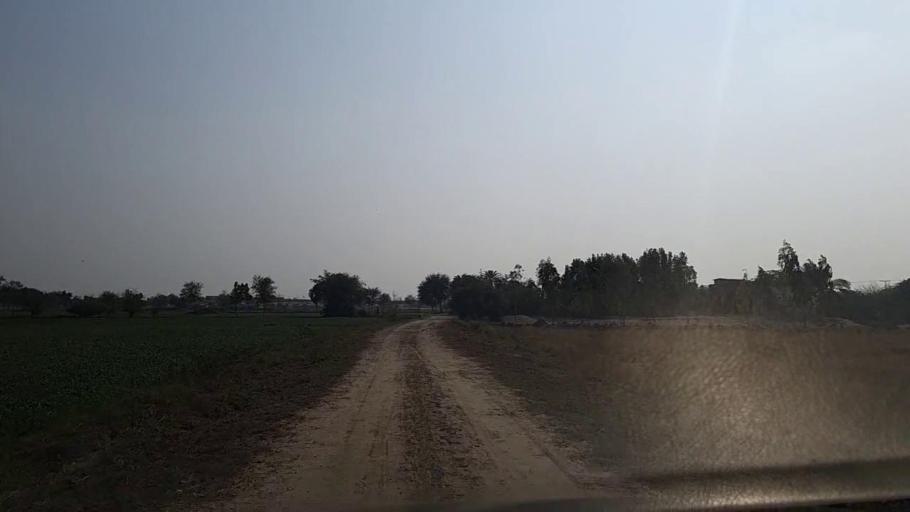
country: PK
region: Sindh
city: Daur
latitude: 26.4014
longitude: 68.4200
